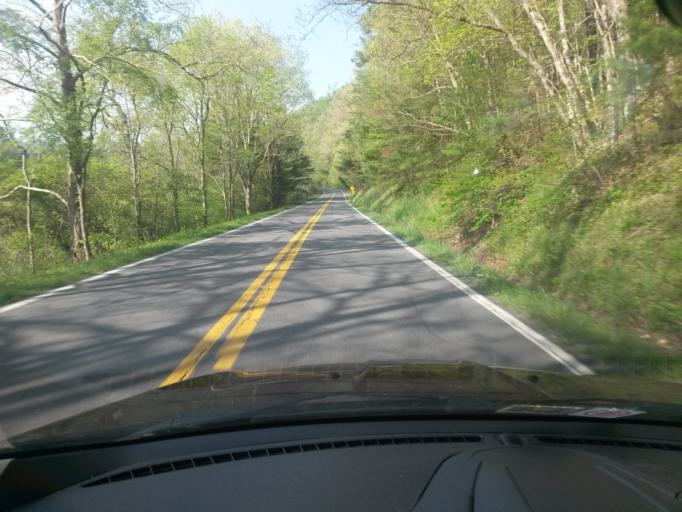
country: US
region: West Virginia
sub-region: Pocahontas County
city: Marlinton
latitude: 38.0035
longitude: -80.0712
